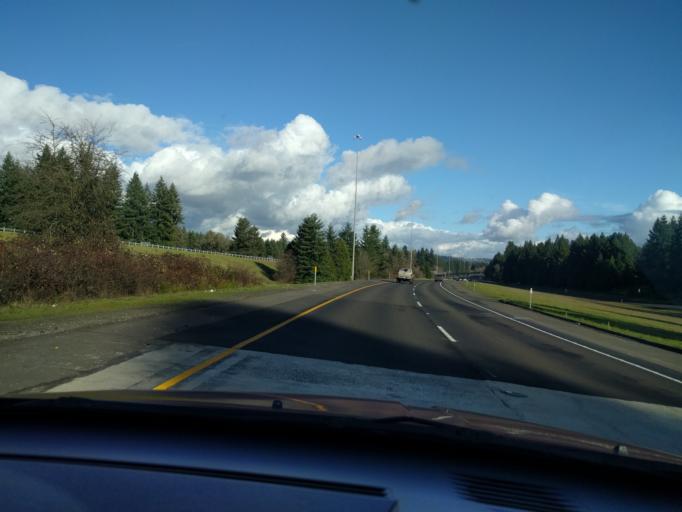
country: US
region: Oregon
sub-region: Washington County
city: Tualatin
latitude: 45.3683
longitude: -122.7561
